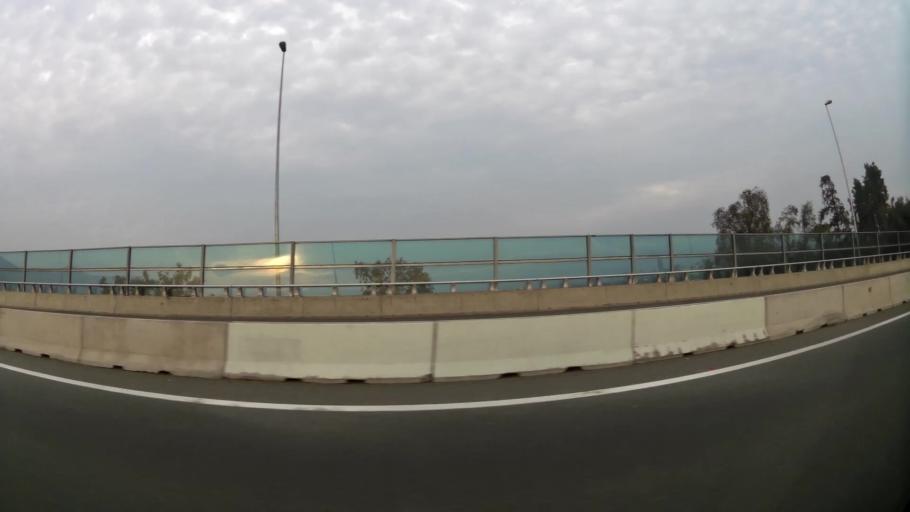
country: CL
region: Santiago Metropolitan
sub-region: Provincia de Santiago
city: Villa Presidente Frei, Nunoa, Santiago, Chile
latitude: -33.3872
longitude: -70.6018
